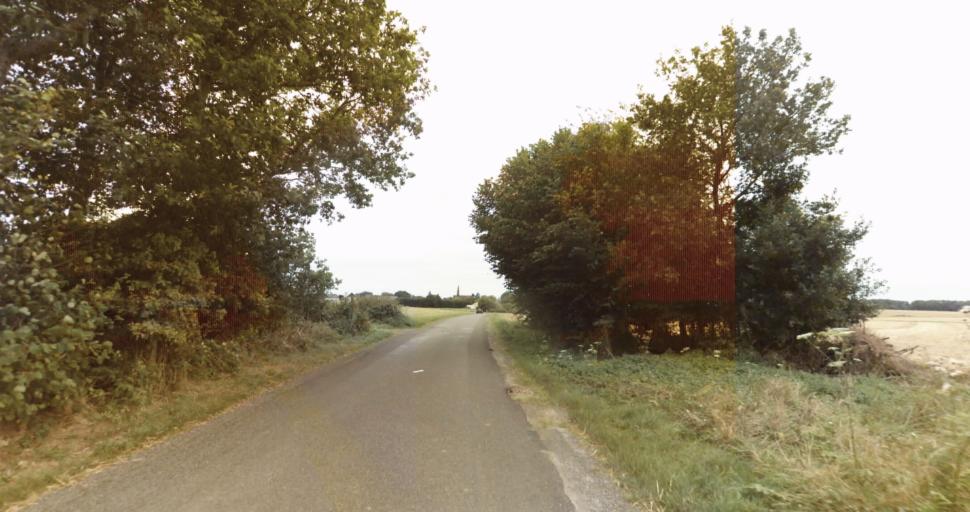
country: FR
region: Haute-Normandie
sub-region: Departement de l'Eure
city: Marcilly-sur-Eure
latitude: 48.9349
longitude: 1.2691
